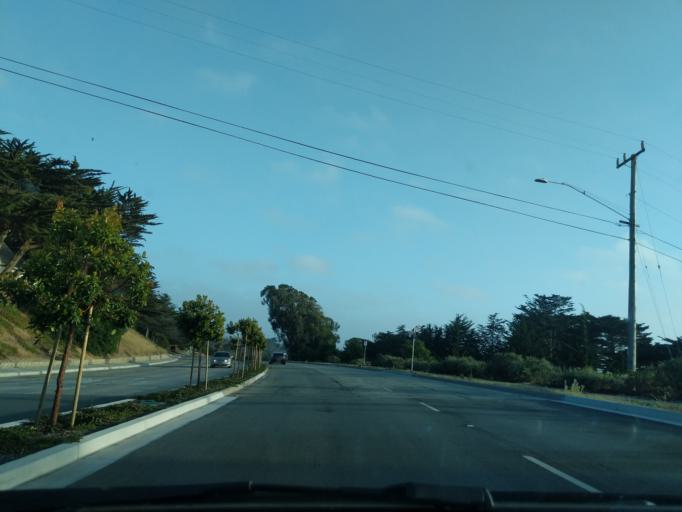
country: US
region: California
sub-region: Monterey County
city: Marina
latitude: 36.6925
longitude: -121.7981
